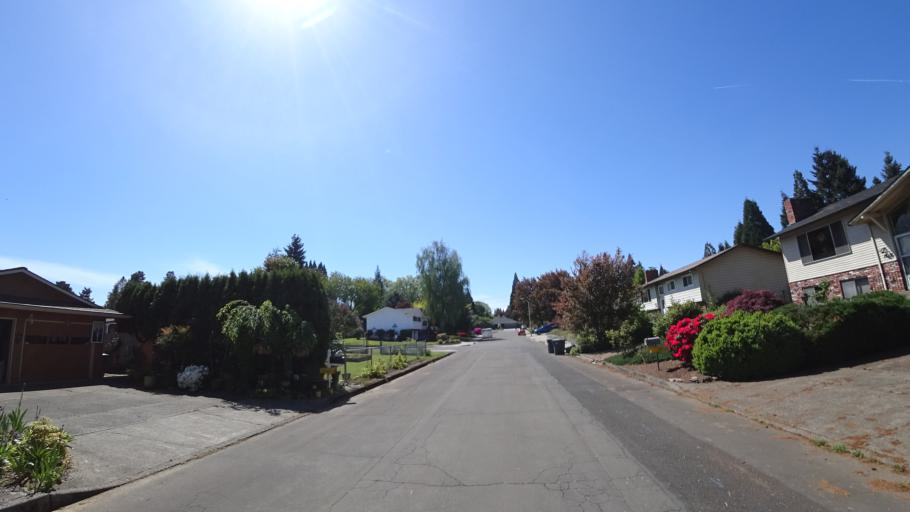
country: US
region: Oregon
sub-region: Washington County
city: Hillsboro
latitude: 45.5135
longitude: -122.9565
